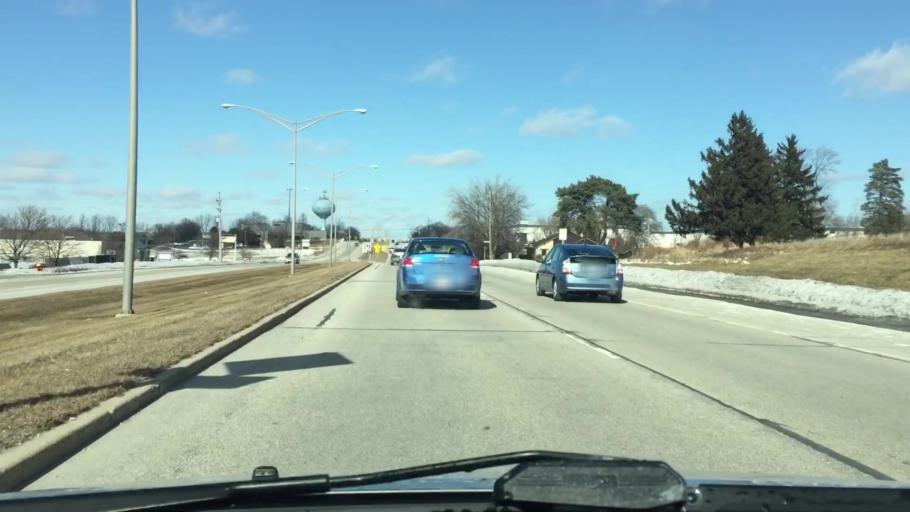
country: US
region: Wisconsin
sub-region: Milwaukee County
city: South Milwaukee
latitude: 42.9051
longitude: -87.9113
